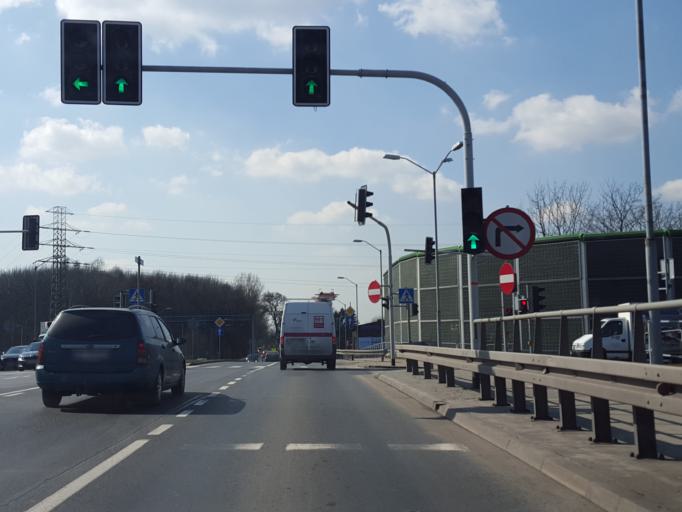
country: PL
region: Silesian Voivodeship
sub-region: Ruda Slaska
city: Ruda Slaska
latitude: 50.2558
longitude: 18.8552
